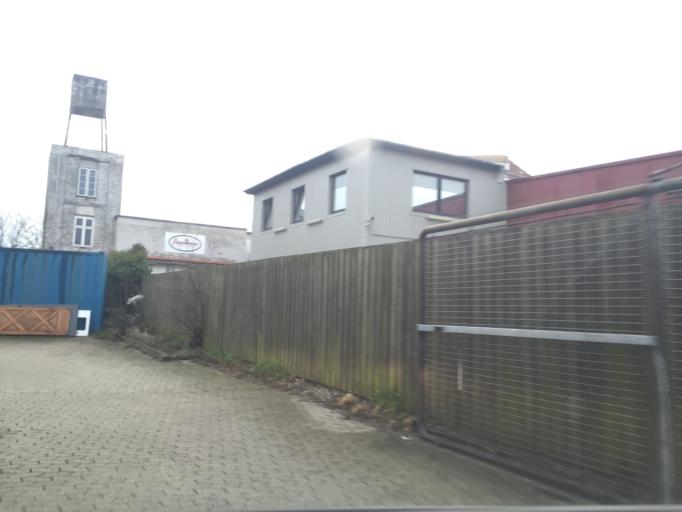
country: DK
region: Capital Region
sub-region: Tarnby Kommune
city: Tarnby
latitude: 55.6154
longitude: 12.6311
